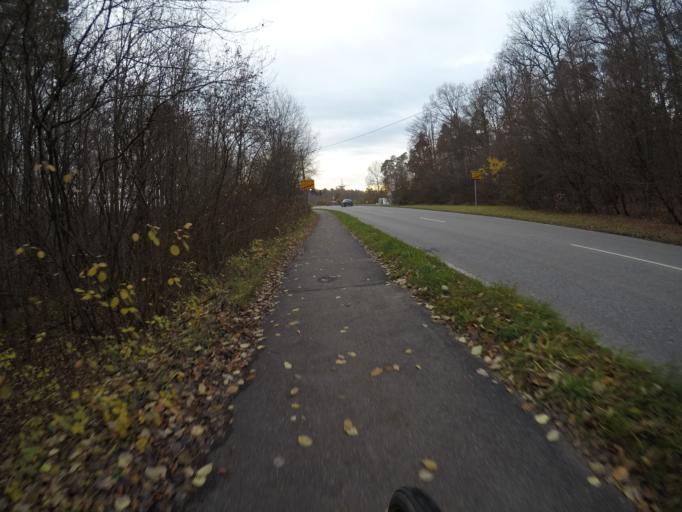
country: DE
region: Baden-Wuerttemberg
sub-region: Regierungsbezirk Stuttgart
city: Steinenbronn
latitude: 48.7125
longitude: 9.1069
